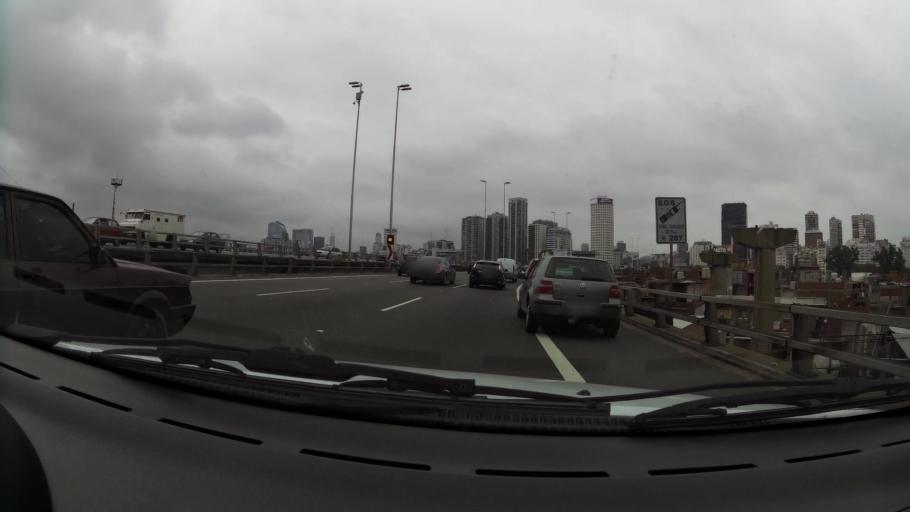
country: AR
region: Buenos Aires F.D.
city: Retiro
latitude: -34.5844
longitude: -58.3800
